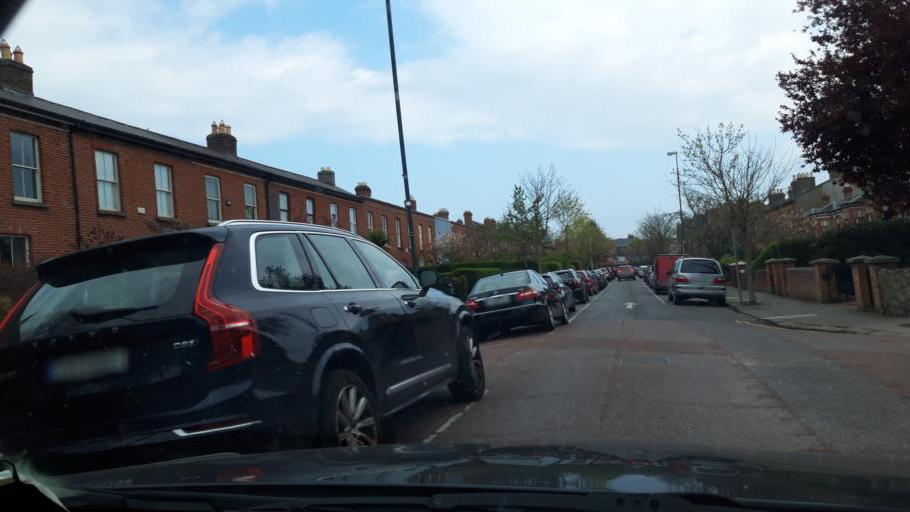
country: IE
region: Leinster
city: Rathmines
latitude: 53.3164
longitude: -6.2681
